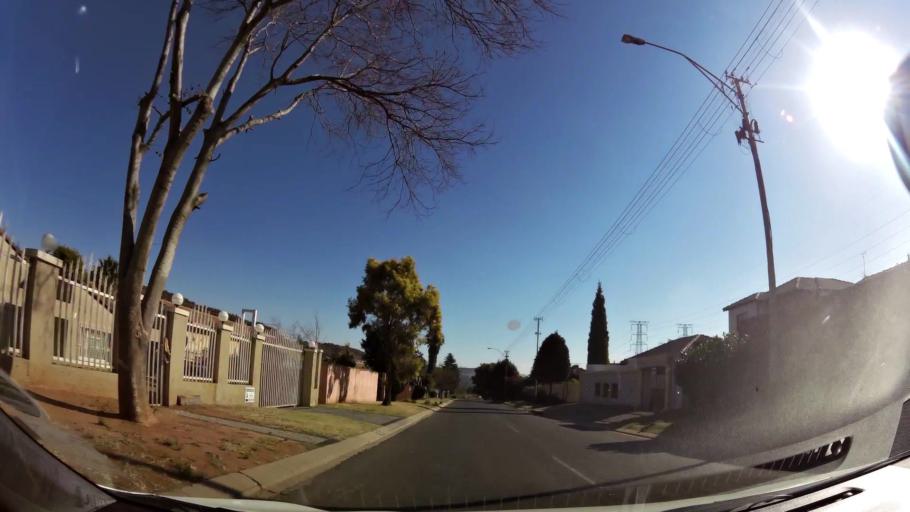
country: ZA
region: Gauteng
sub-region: City of Johannesburg Metropolitan Municipality
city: Johannesburg
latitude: -26.2761
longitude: 28.0290
